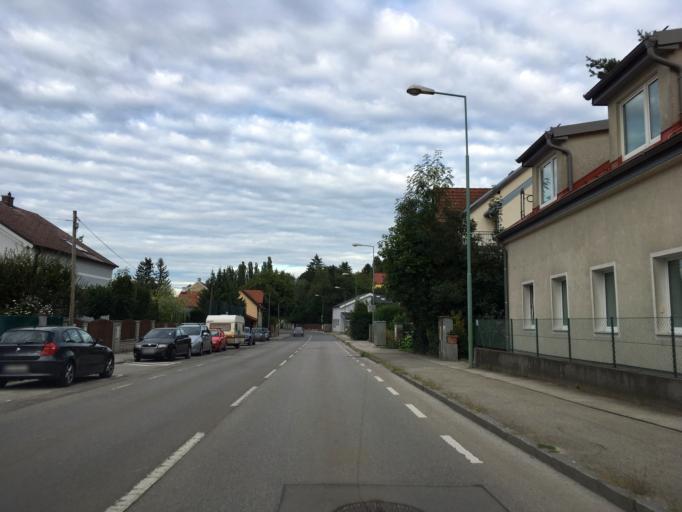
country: AT
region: Lower Austria
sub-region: Politischer Bezirk Tulln
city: Wordern
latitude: 48.3078
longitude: 16.2636
